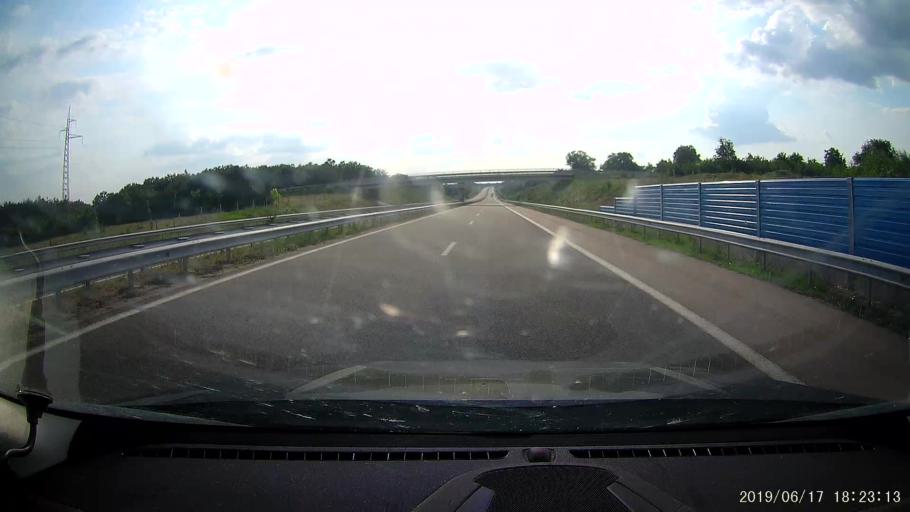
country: BG
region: Khaskovo
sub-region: Obshtina Simeonovgrad
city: Simeonovgrad
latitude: 41.9747
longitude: 25.7285
